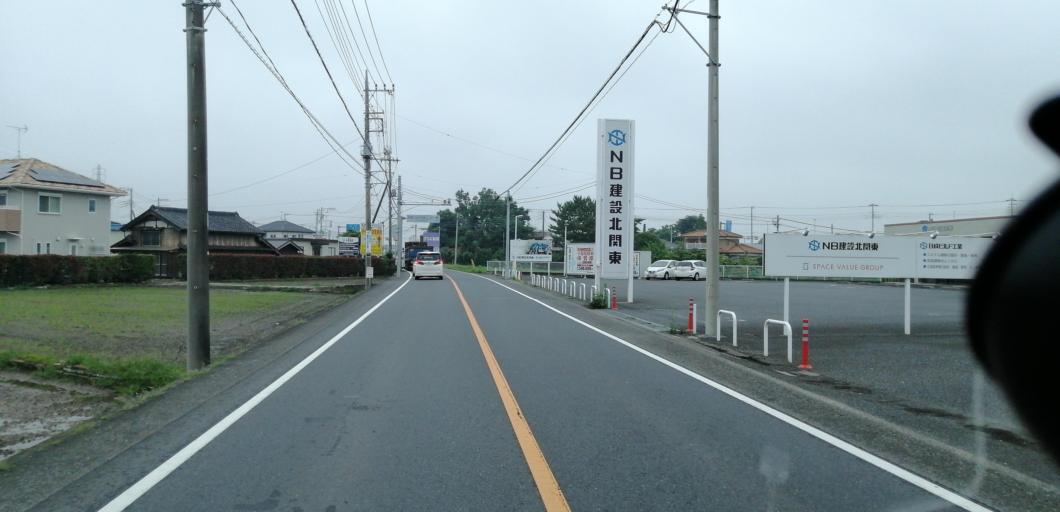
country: JP
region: Saitama
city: Kazo
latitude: 36.1224
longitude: 139.6249
